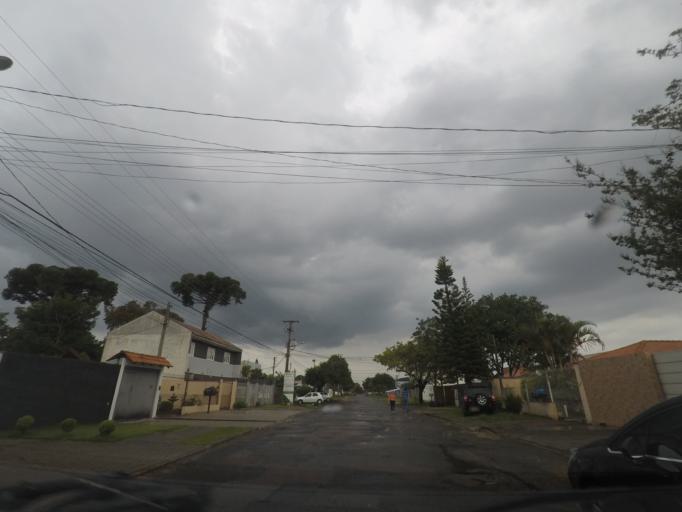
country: BR
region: Parana
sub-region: Sao Jose Dos Pinhais
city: Sao Jose dos Pinhais
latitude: -25.4815
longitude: -49.2419
